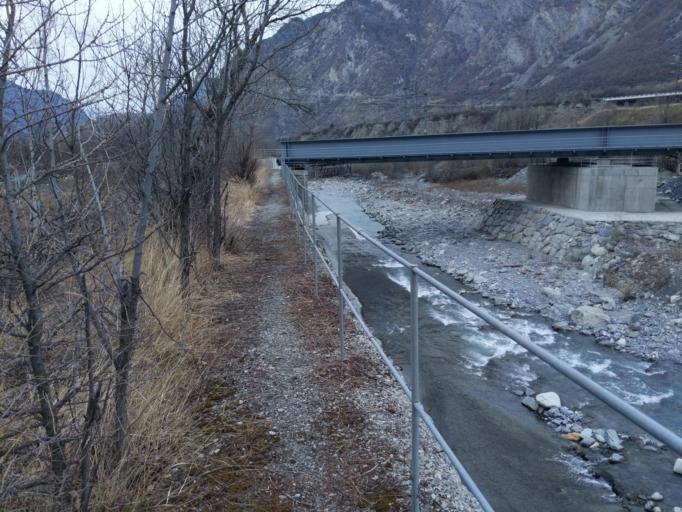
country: FR
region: Rhone-Alpes
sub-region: Departement de la Savoie
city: Villargondran
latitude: 45.2512
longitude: 6.3911
